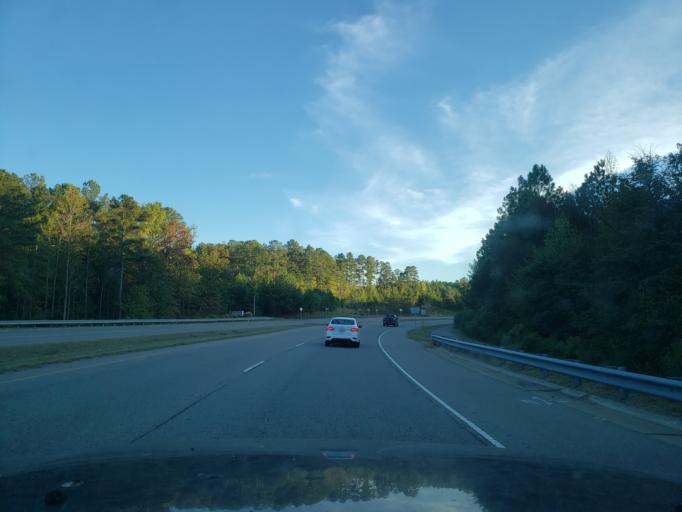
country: US
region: North Carolina
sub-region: Wake County
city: Morrisville
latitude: 35.8442
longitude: -78.8545
